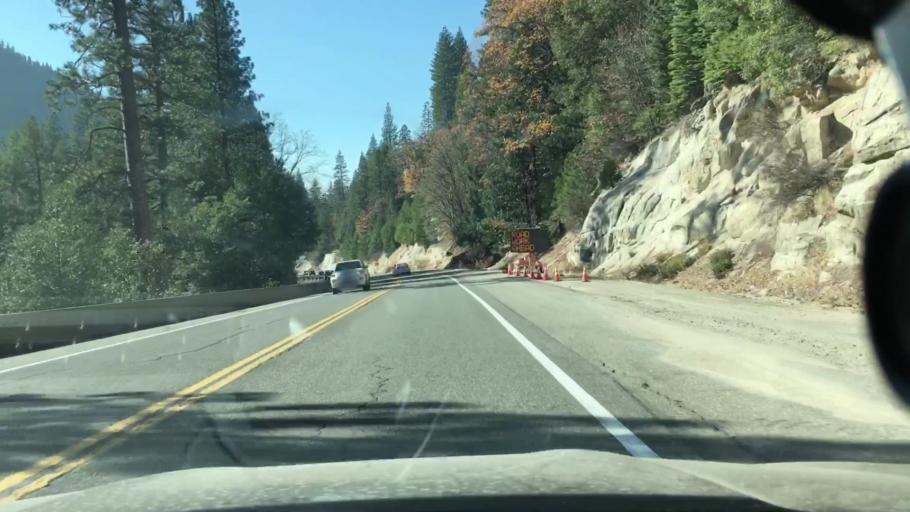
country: US
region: California
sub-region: El Dorado County
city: South Lake Tahoe
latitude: 38.7780
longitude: -120.2593
